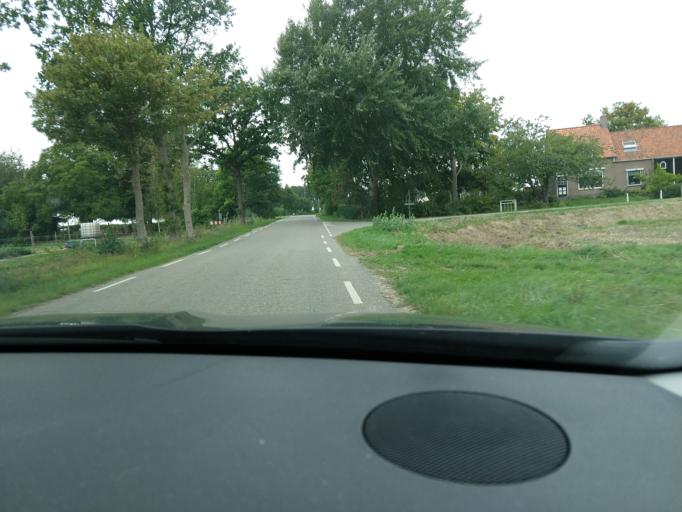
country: NL
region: Zeeland
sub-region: Gemeente Terneuzen
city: Terneuzen
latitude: 51.4140
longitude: 3.8422
